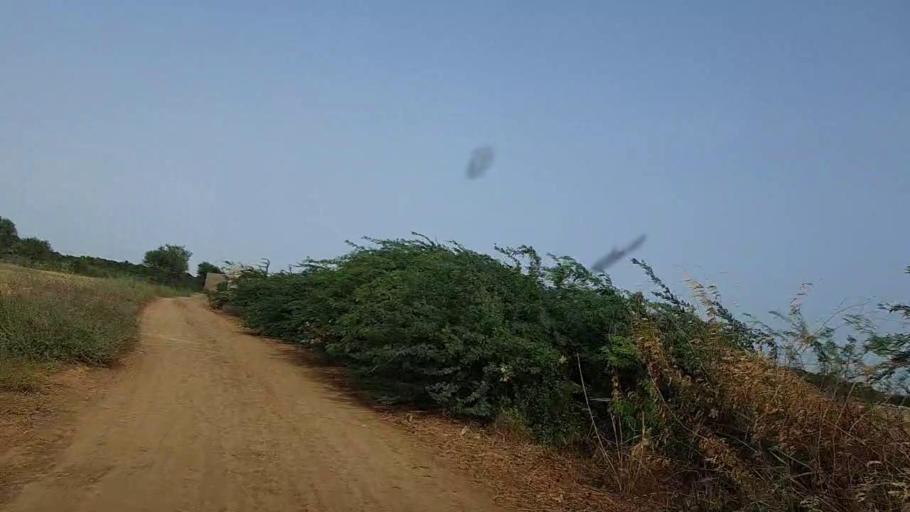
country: PK
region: Sindh
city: Kotri
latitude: 25.2400
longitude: 68.2433
